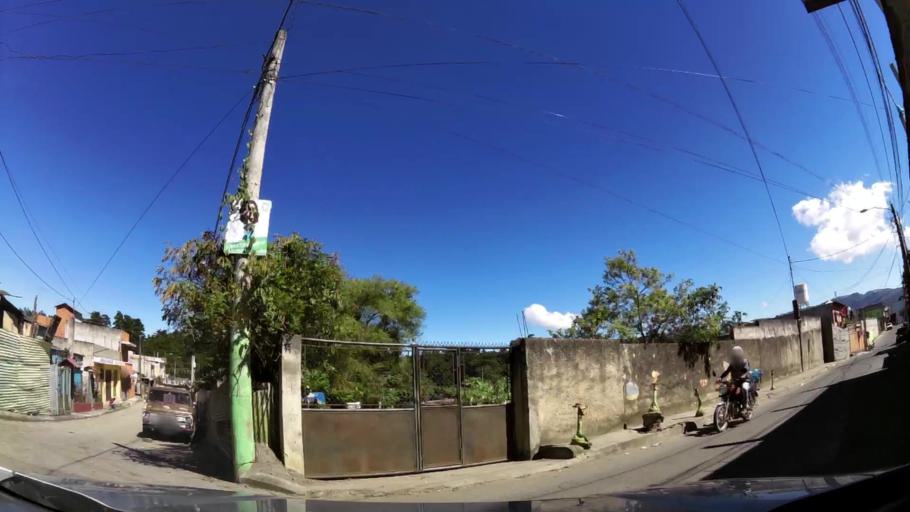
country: GT
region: Guatemala
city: San Jose Pinula
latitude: 14.5483
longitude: -90.4126
